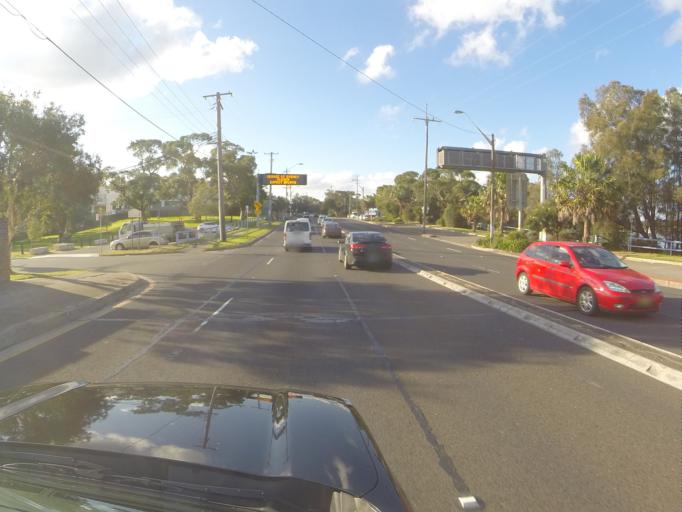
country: AU
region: New South Wales
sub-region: Kogarah
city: Blakehurst
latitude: -33.9978
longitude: 151.1159
